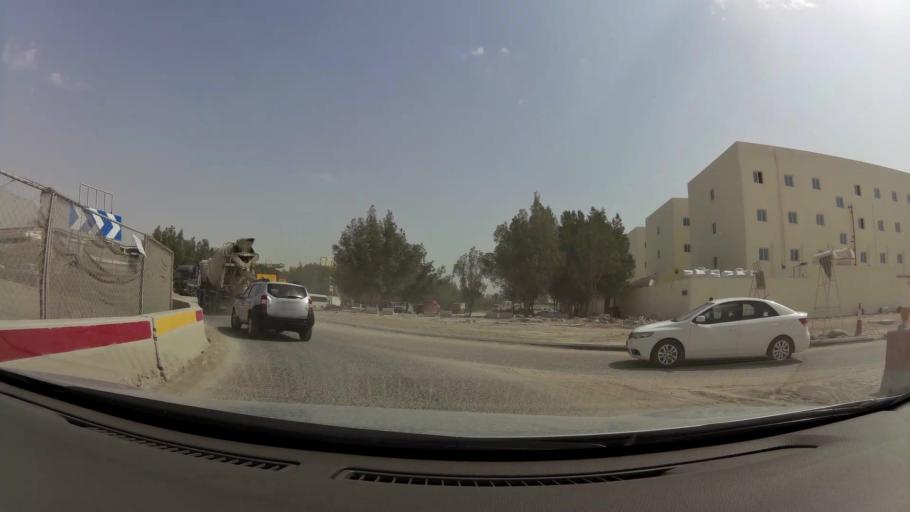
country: QA
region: Al Wakrah
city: Al Wukayr
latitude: 25.1758
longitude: 51.4461
